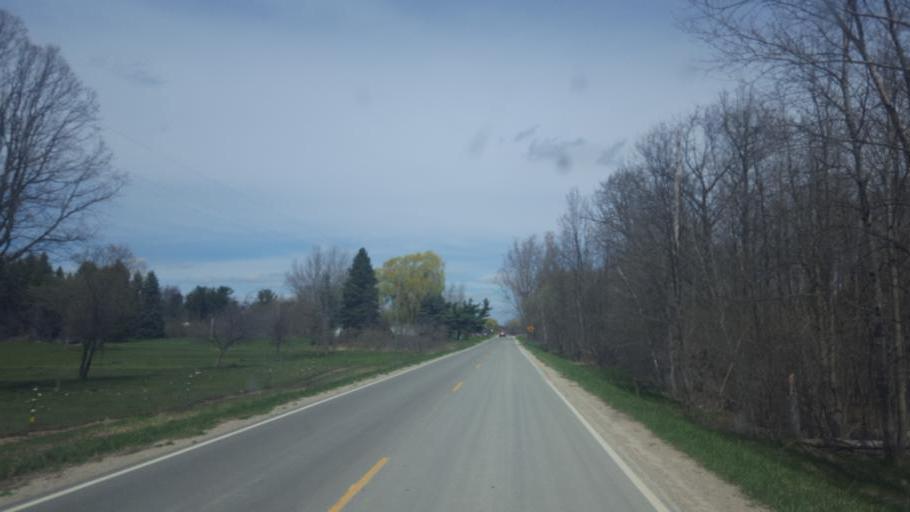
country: US
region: Michigan
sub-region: Isabella County
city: Lake Isabella
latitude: 43.5936
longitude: -84.9474
